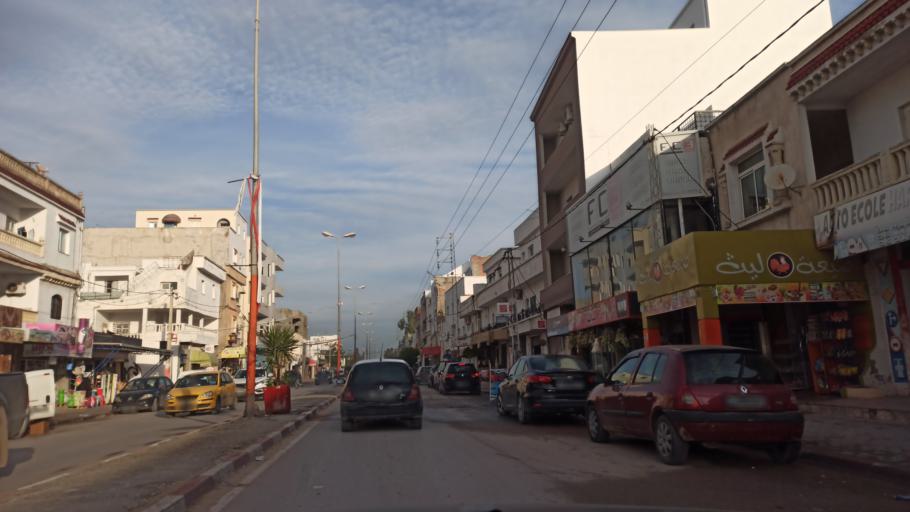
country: TN
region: Ariana
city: Ariana
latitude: 36.8658
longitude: 10.2518
